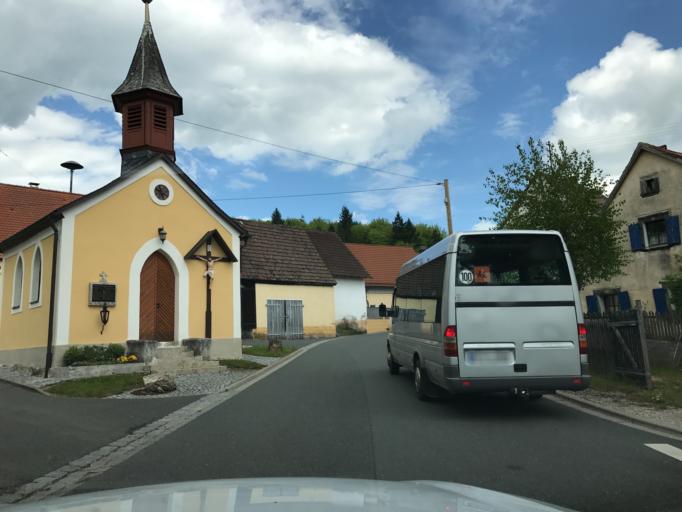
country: DE
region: Bavaria
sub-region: Upper Franconia
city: Egloffstein
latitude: 49.7111
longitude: 11.2161
